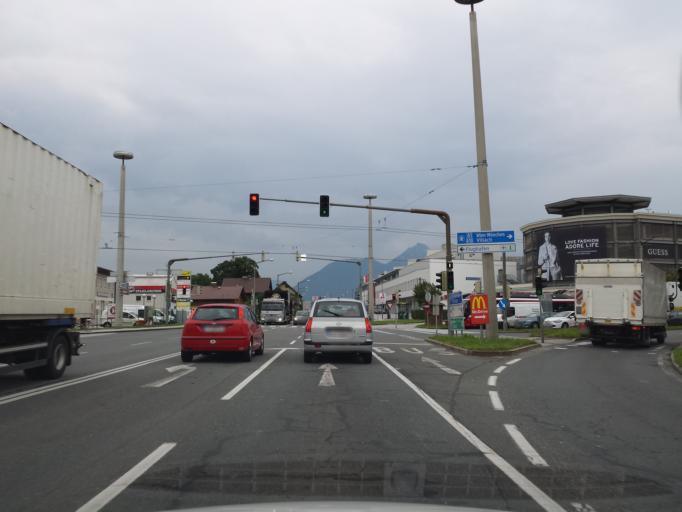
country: DE
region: Bavaria
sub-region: Upper Bavaria
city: Ainring
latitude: 47.7924
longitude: 12.9924
